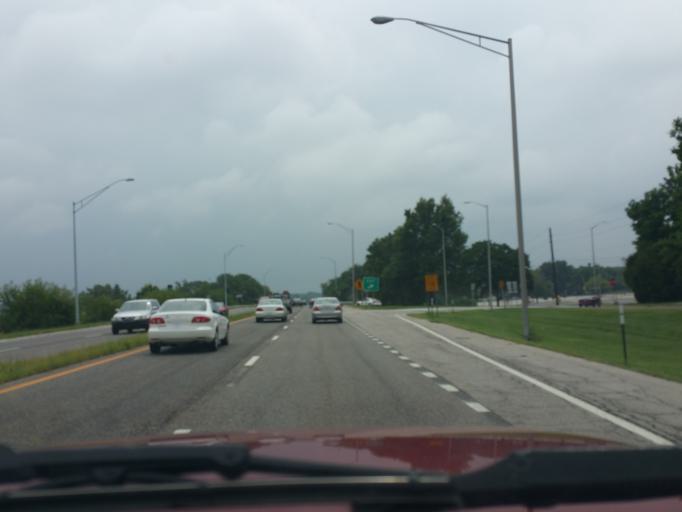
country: US
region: Kansas
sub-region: Johnson County
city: Mission
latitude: 39.0242
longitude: -94.6678
